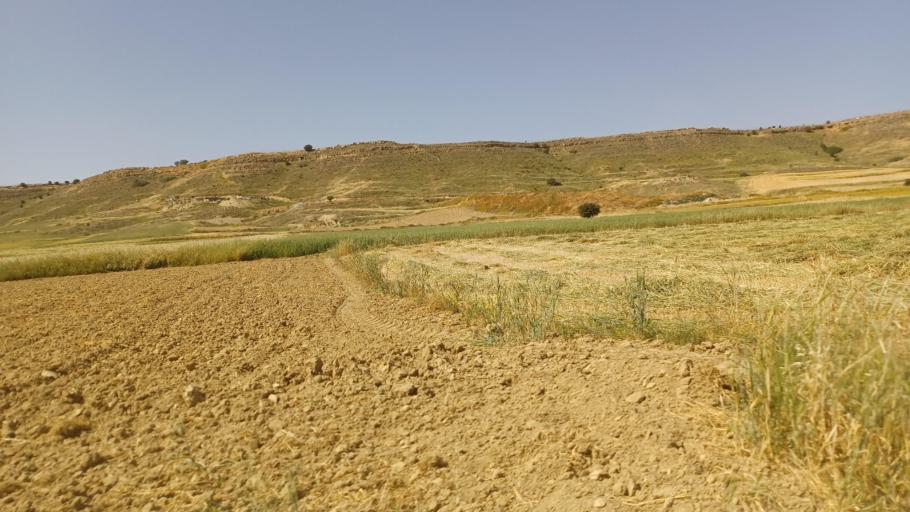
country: CY
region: Lefkosia
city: Mammari
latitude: 35.1725
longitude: 33.2247
